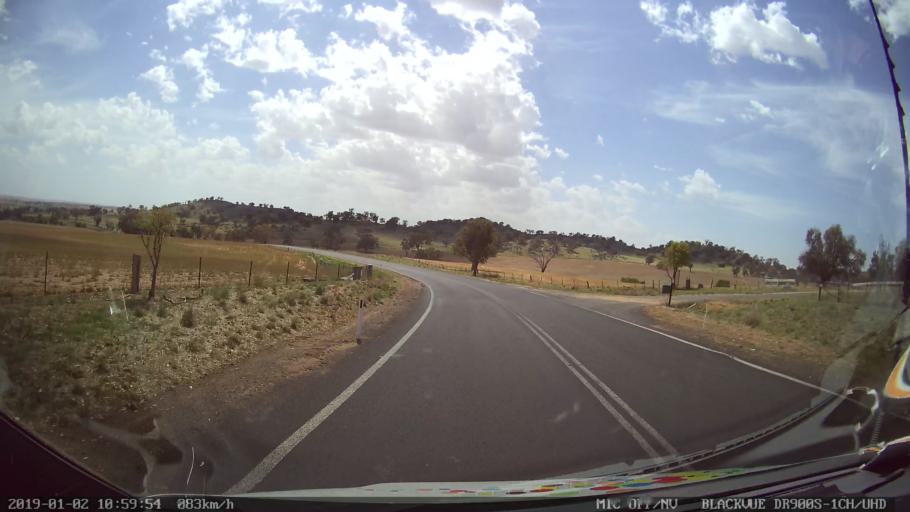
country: AU
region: New South Wales
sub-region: Cootamundra
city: Cootamundra
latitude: -34.6110
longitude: 148.3109
